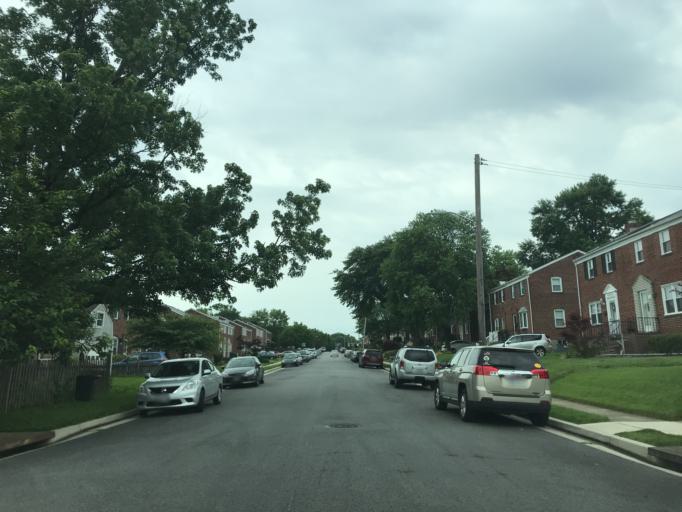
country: US
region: Maryland
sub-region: Baltimore County
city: Overlea
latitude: 39.3595
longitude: -76.5124
